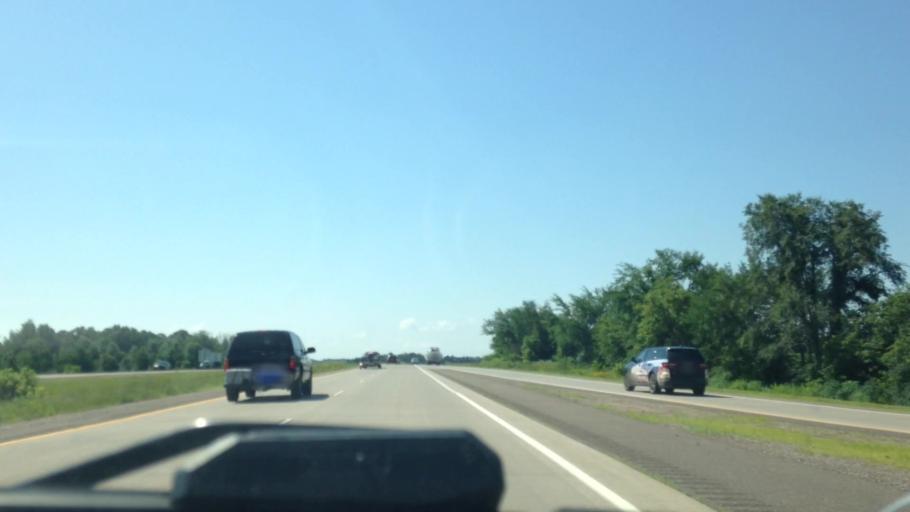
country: US
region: Wisconsin
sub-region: Barron County
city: Rice Lake
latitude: 45.4704
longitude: -91.7585
